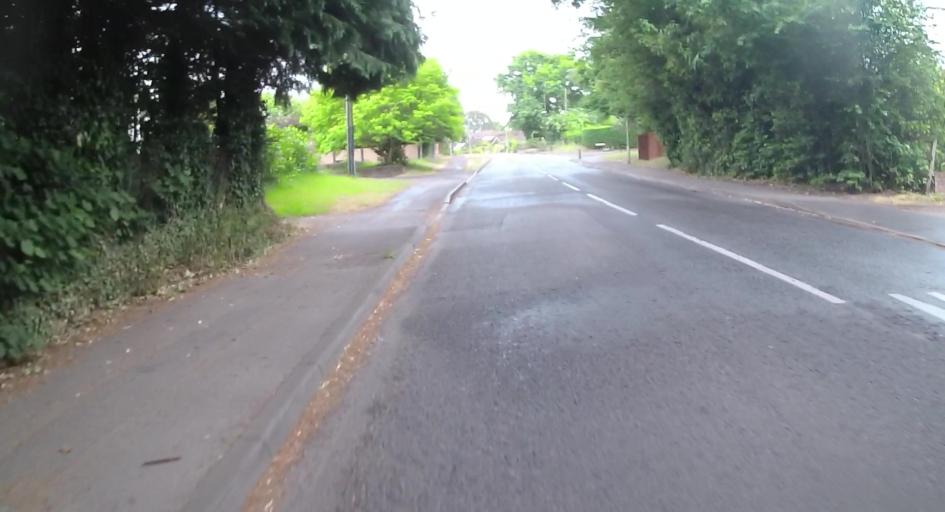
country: GB
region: England
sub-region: Hampshire
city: Fleet
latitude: 51.2646
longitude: -0.8540
